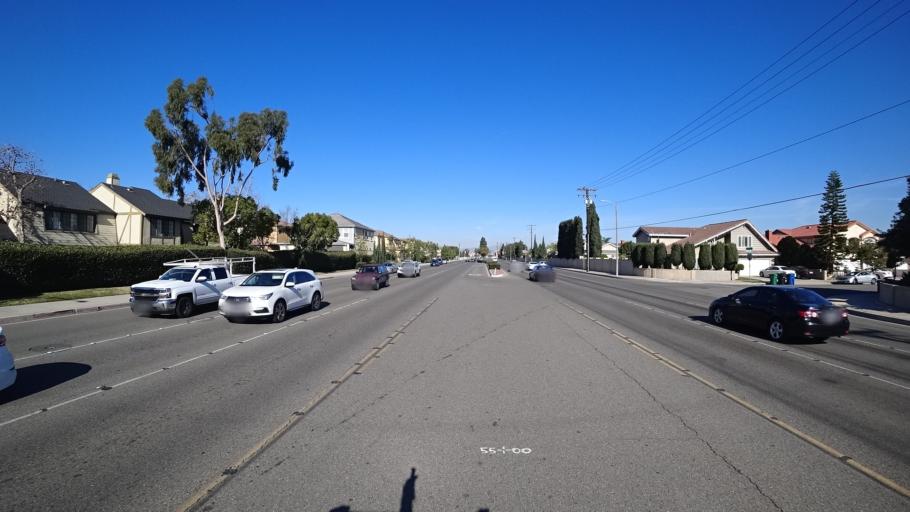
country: US
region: California
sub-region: Orange County
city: Garden Grove
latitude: 33.7464
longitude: -117.9549
